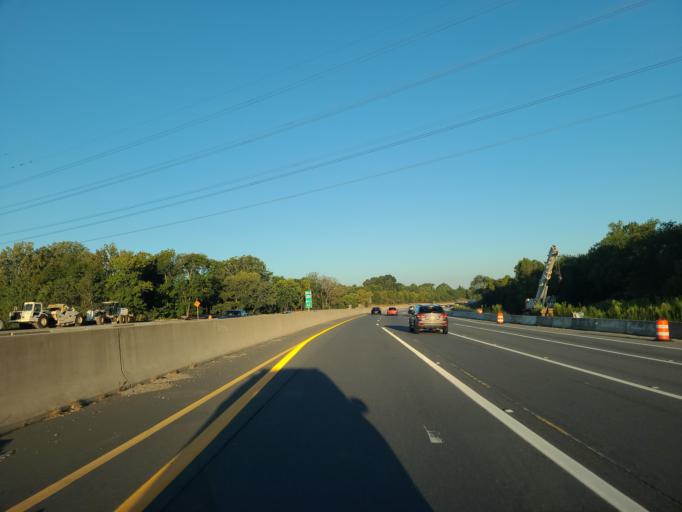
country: US
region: North Carolina
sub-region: Mecklenburg County
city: Pineville
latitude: 35.0653
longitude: -80.8562
